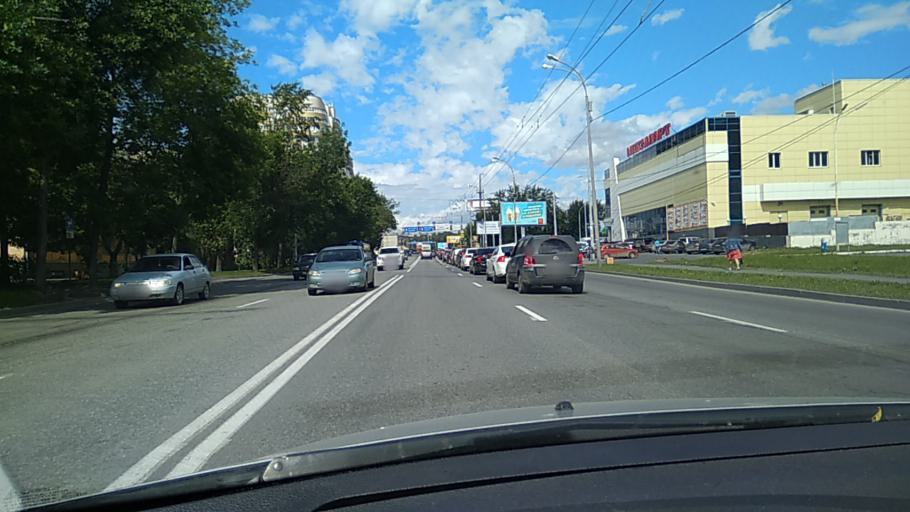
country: RU
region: Sverdlovsk
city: Yekaterinburg
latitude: 56.9125
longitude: 60.6119
